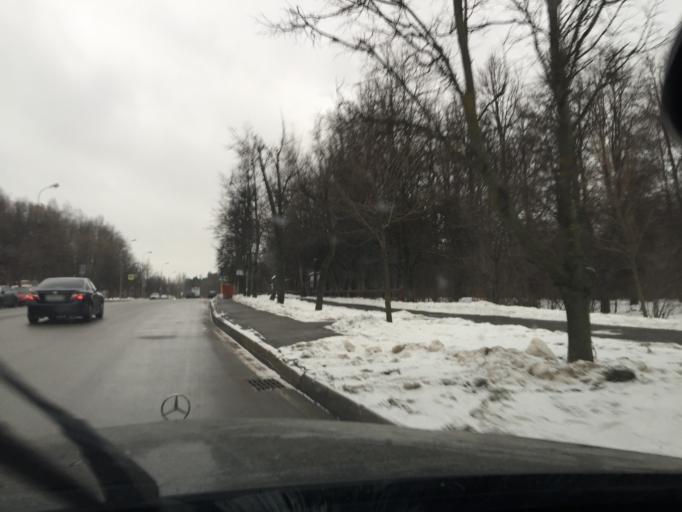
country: RU
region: Moscow
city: Troparevo
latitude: 55.6467
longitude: 37.4687
